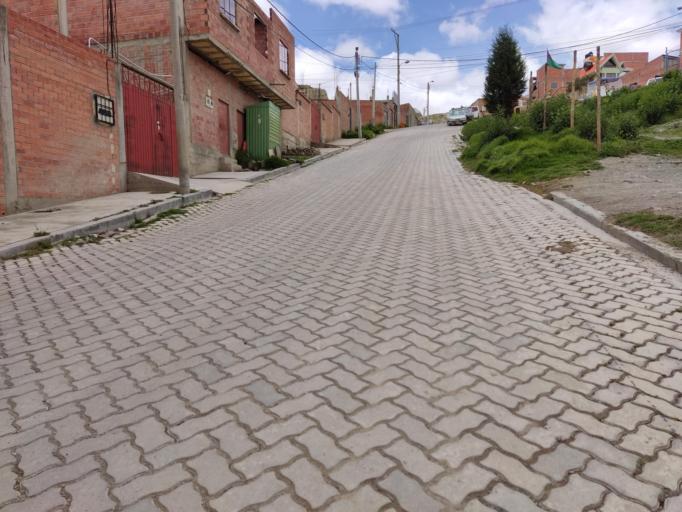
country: BO
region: La Paz
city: La Paz
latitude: -16.5346
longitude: -68.1310
